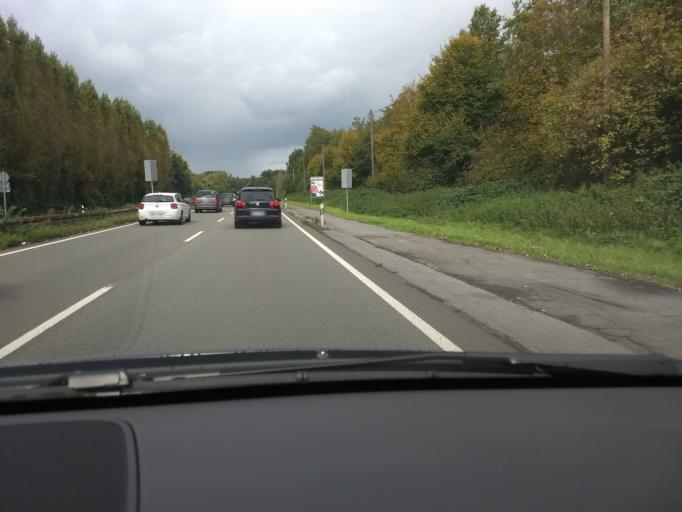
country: DE
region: North Rhine-Westphalia
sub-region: Regierungsbezirk Munster
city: Gladbeck
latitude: 51.5250
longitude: 6.9904
